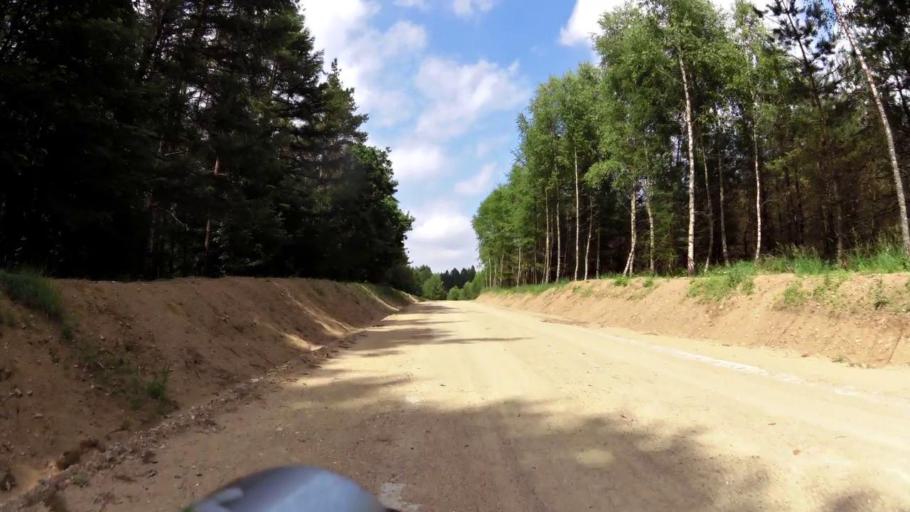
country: PL
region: West Pomeranian Voivodeship
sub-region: Powiat szczecinecki
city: Bialy Bor
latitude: 53.9551
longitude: 16.7580
